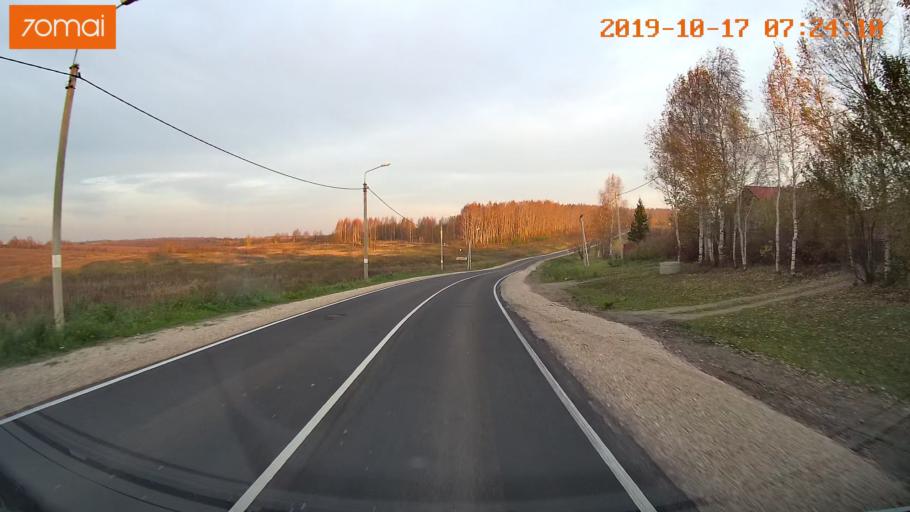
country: RU
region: Ivanovo
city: Gavrilov Posad
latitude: 56.3352
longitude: 40.1144
